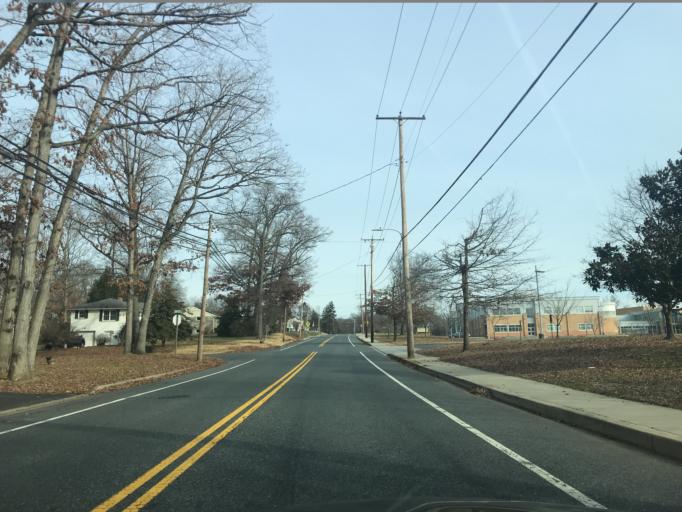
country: US
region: Maryland
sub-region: Harford County
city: Aberdeen
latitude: 39.5148
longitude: -76.1738
